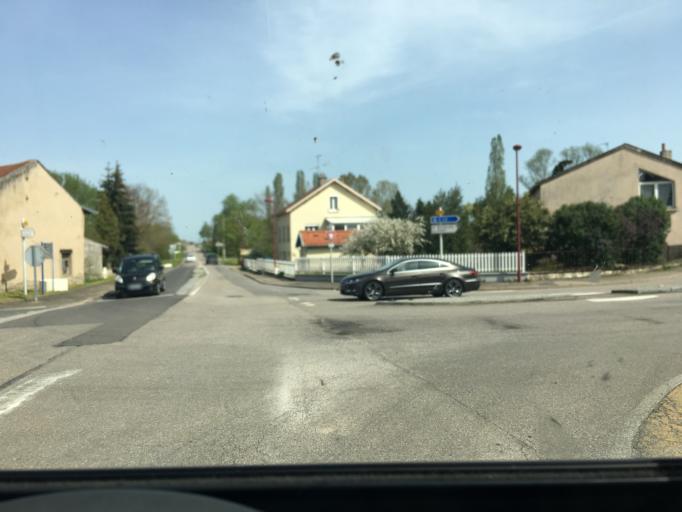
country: FR
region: Lorraine
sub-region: Departement de Meurthe-et-Moselle
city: Art-sur-Meurthe
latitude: 48.6160
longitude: 6.2541
